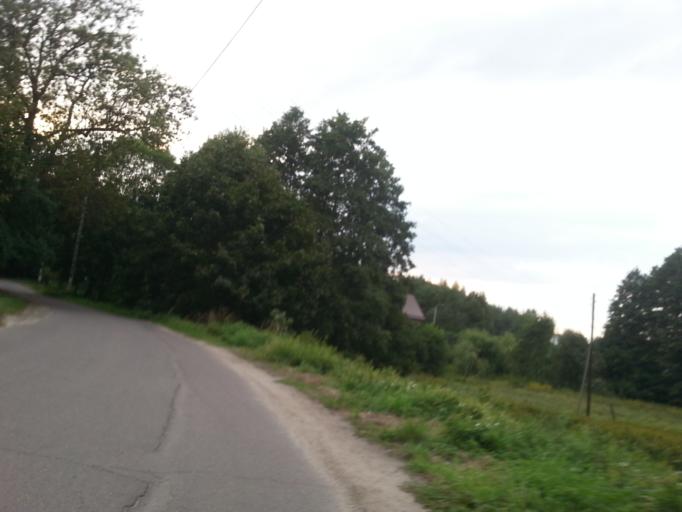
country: PL
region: Lower Silesian Voivodeship
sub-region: Powiat olesnicki
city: Twardogora
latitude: 51.3698
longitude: 17.4644
